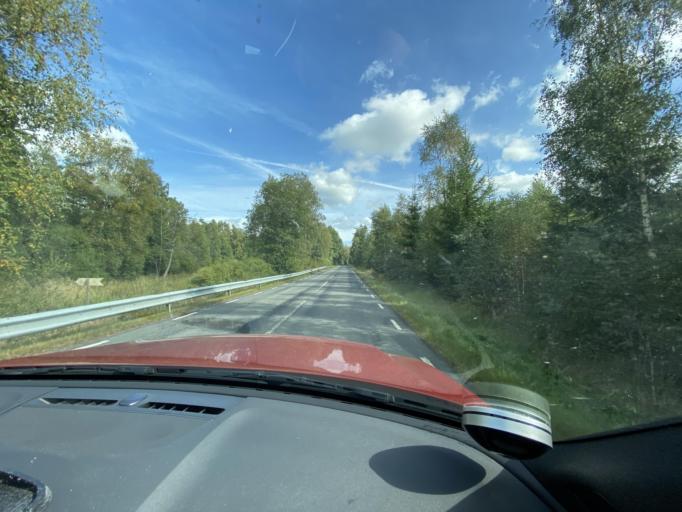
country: SE
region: Skane
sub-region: Hassleholms Kommun
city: Bjarnum
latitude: 56.3557
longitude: 13.7483
